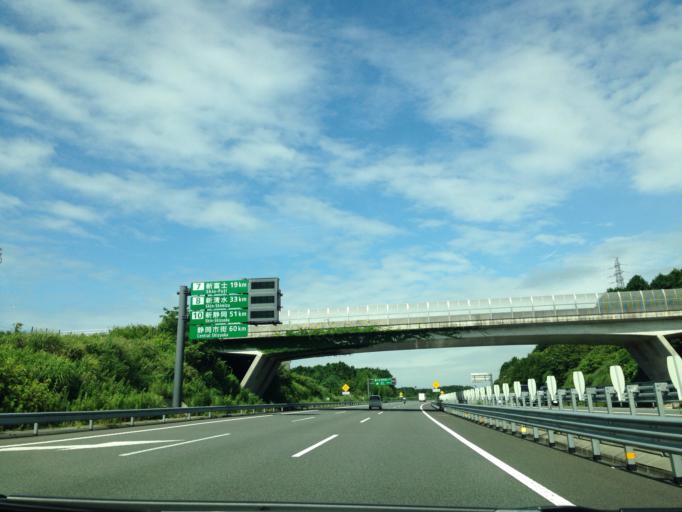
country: JP
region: Shizuoka
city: Numazu
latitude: 35.1521
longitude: 138.8510
